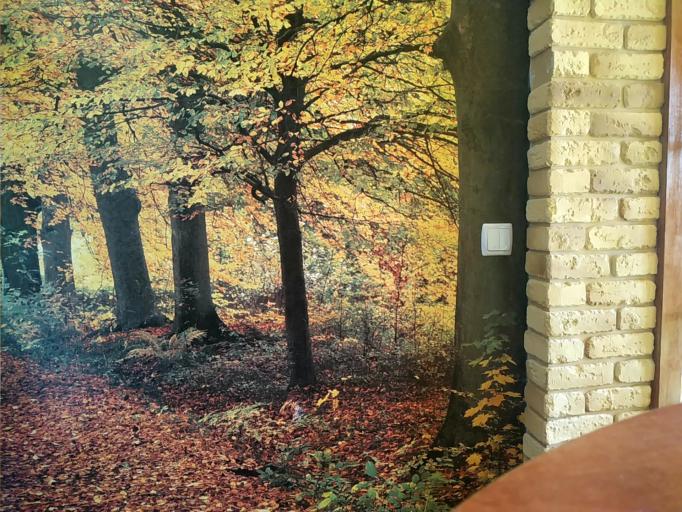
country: RU
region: Jaroslavl
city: Kukoboy
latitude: 58.9155
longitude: 39.6804
